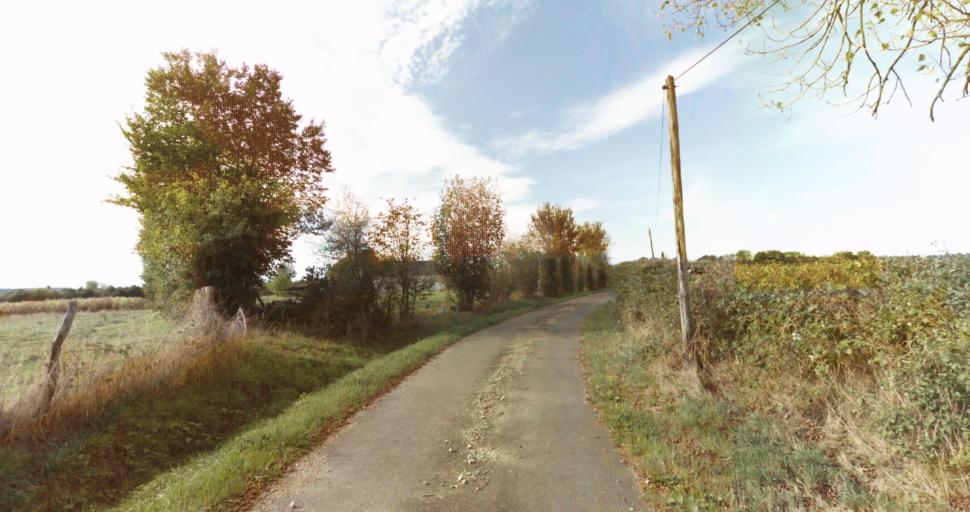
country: FR
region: Lower Normandy
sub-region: Departement de l'Orne
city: Gace
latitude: 48.7099
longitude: 0.2566
